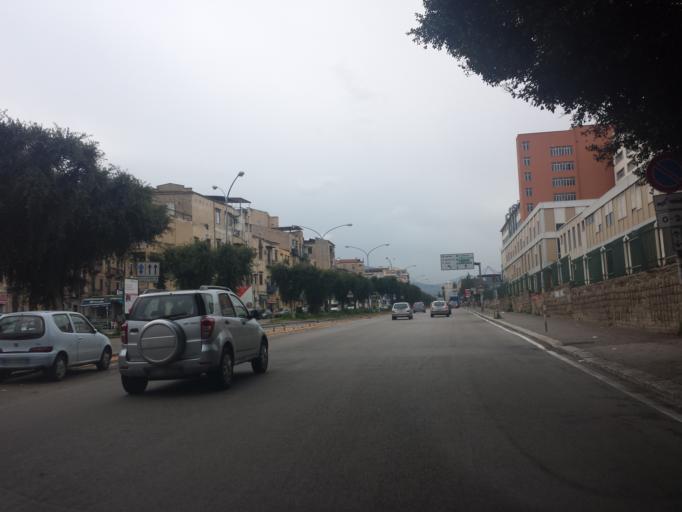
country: IT
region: Sicily
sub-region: Palermo
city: Palermo
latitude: 38.1074
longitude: 13.3536
